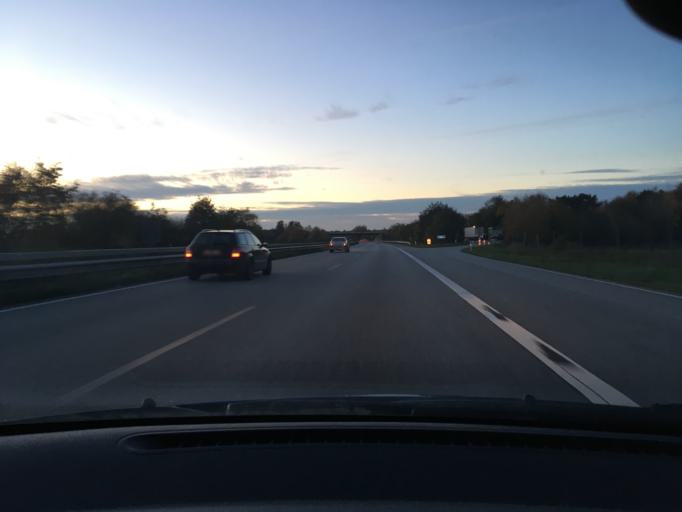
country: DE
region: Schleswig-Holstein
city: Datgen
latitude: 54.1872
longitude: 9.9354
